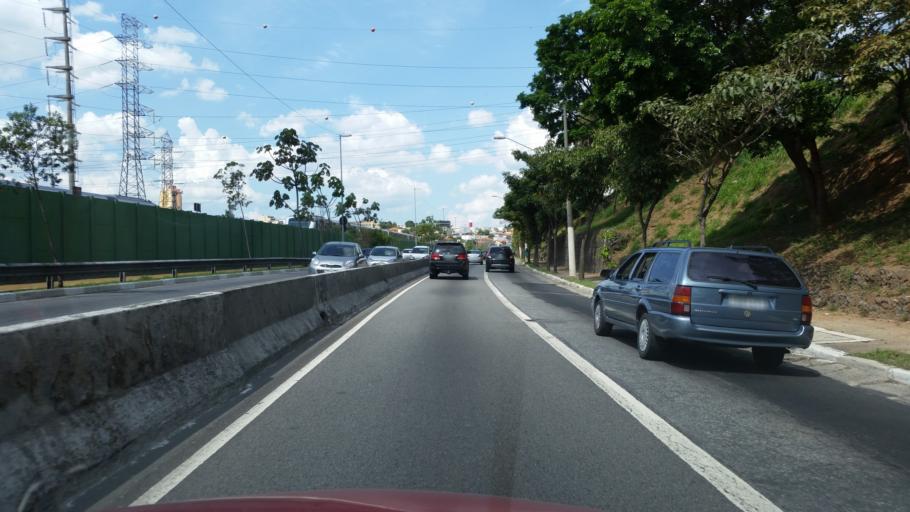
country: BR
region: Sao Paulo
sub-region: Guarulhos
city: Guarulhos
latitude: -23.5284
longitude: -46.5138
